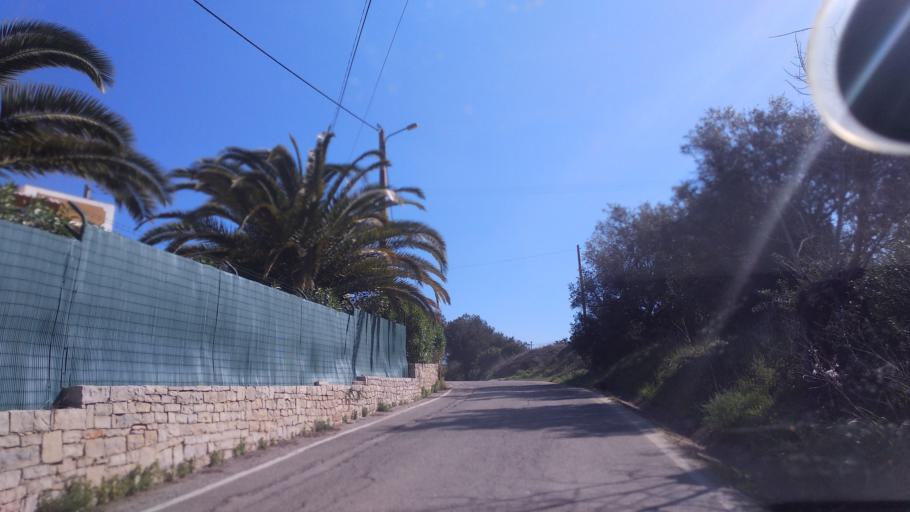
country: PT
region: Faro
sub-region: Faro
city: Santa Barbara de Nexe
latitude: 37.1119
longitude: -7.9249
